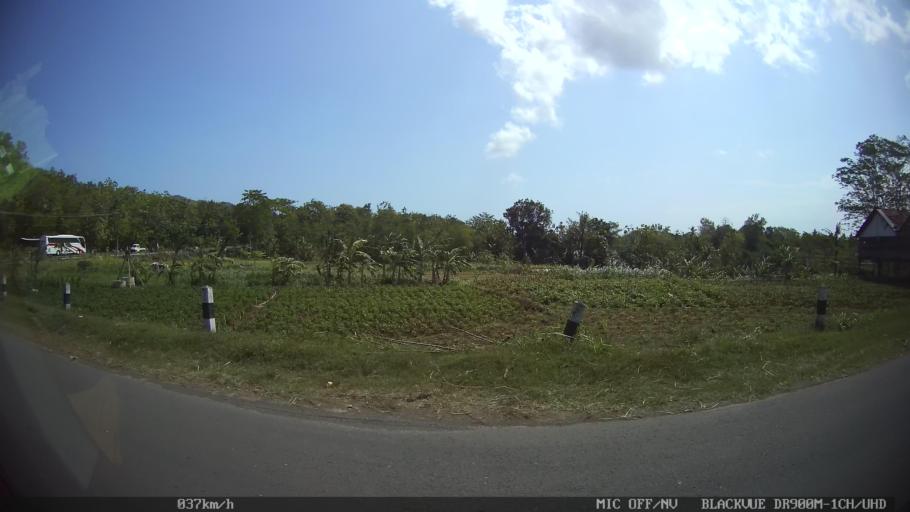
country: ID
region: Daerah Istimewa Yogyakarta
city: Pundong
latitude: -7.9759
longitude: 110.3474
